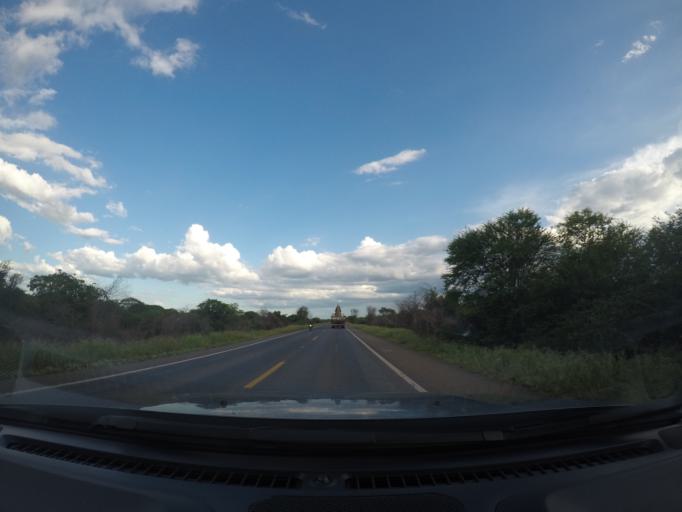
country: BR
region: Bahia
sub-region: Oliveira Dos Brejinhos
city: Beira Rio
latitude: -12.2080
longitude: -42.8053
